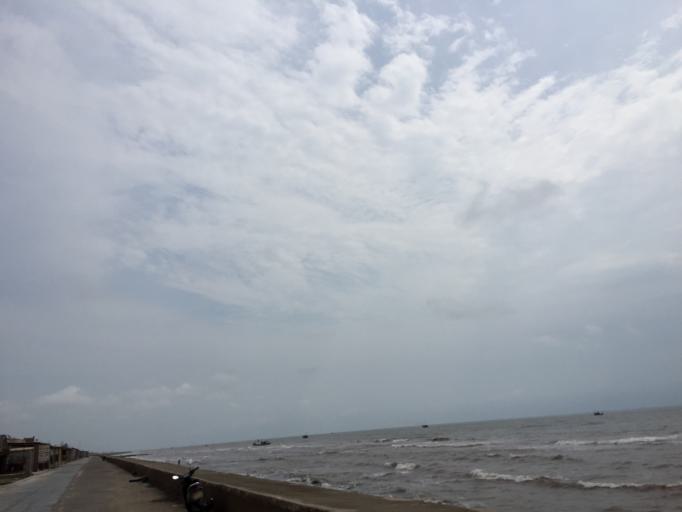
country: VN
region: Ninh Binh
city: Thi Tran Phat Diem
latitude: 20.0307
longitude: 106.2243
